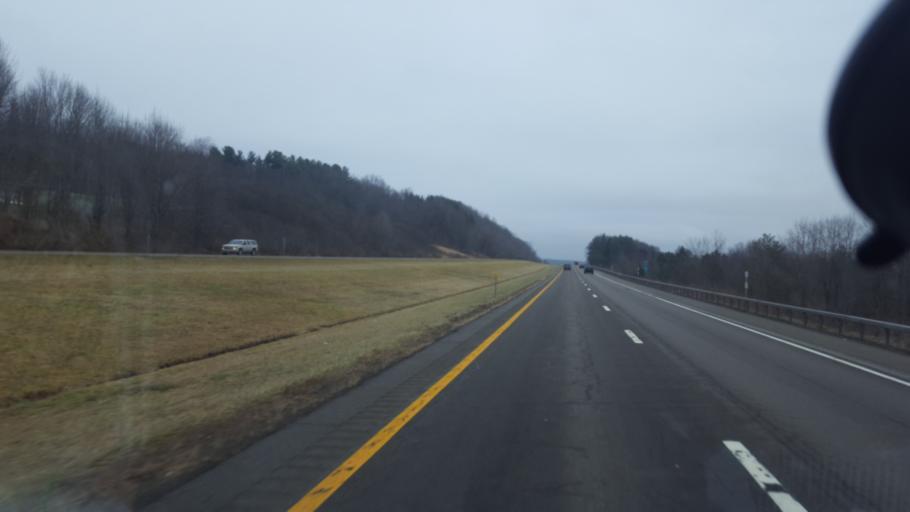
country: US
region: New York
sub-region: Chautauqua County
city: Falconer
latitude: 42.1367
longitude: -79.1254
